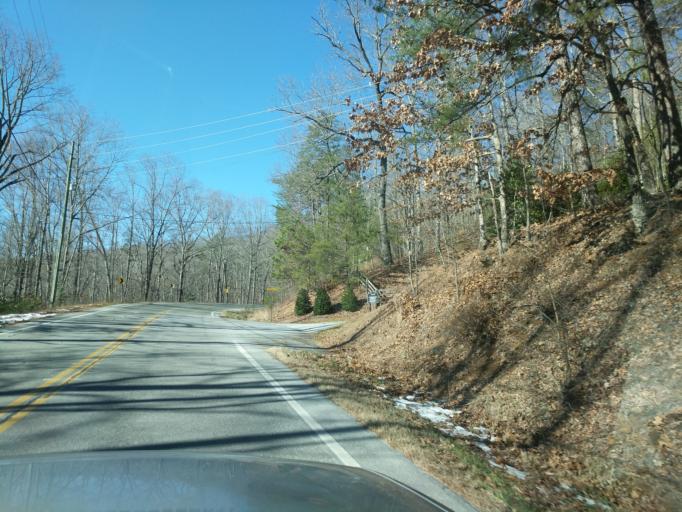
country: US
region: Georgia
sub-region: Rabun County
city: Clayton
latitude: 34.8720
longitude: -83.5499
